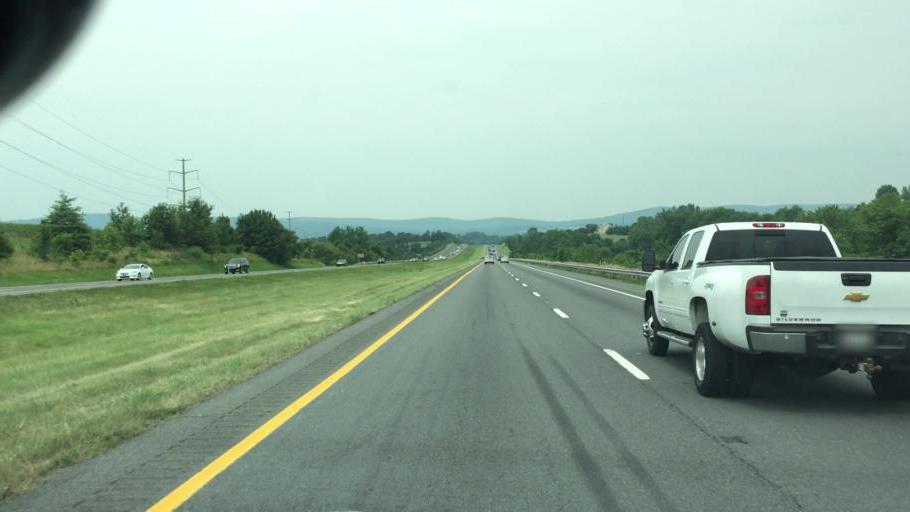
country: US
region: Maryland
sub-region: Frederick County
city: Middletown
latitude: 39.4659
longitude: -77.5193
